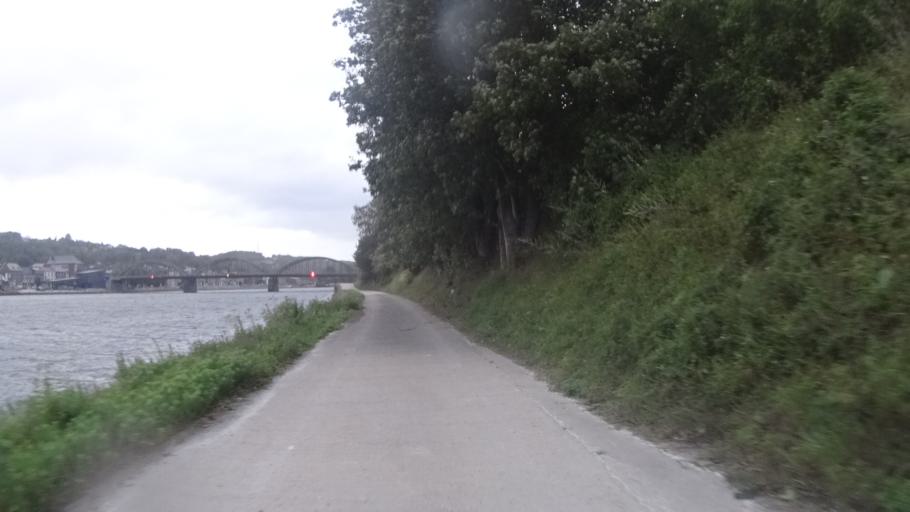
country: BE
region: Wallonia
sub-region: Province de Liege
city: Engis
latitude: 50.5785
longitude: 5.4030
